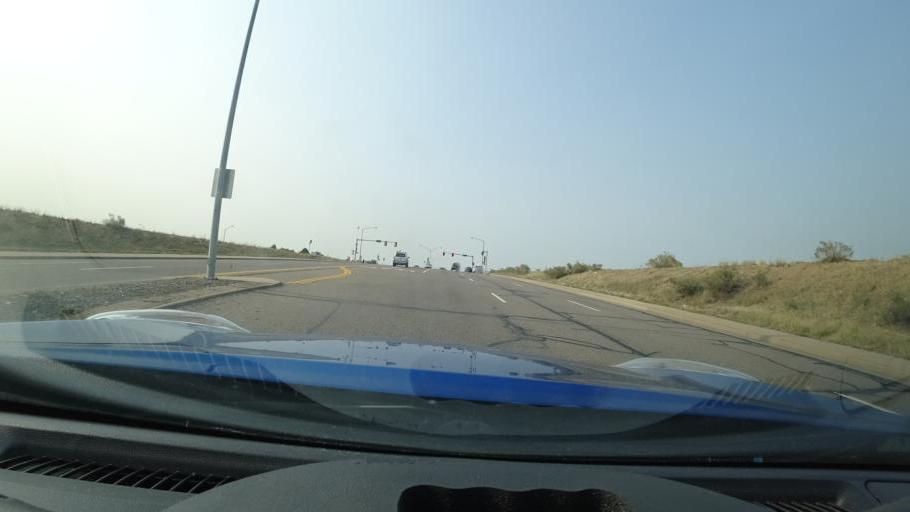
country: US
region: Colorado
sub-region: Adams County
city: Aurora
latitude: 39.6695
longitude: -104.8099
